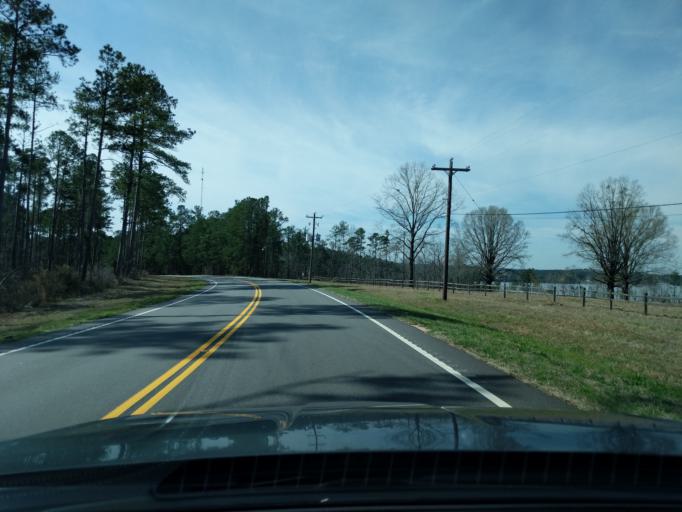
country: US
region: Georgia
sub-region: Columbia County
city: Evans
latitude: 33.6688
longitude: -82.1870
